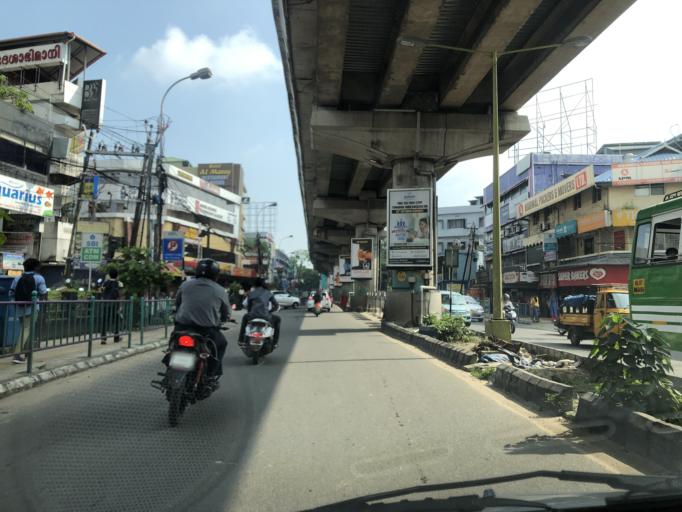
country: IN
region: Kerala
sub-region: Ernakulam
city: Cochin
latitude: 9.9982
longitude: 76.2962
